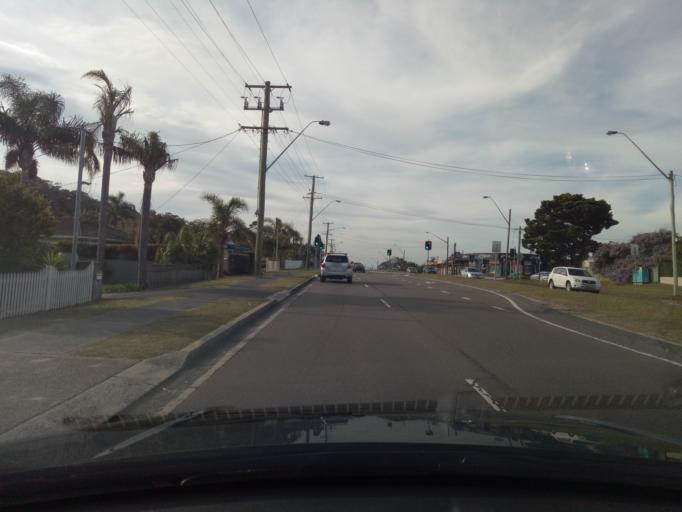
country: AU
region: New South Wales
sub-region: Wyong Shire
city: Bateau Bay
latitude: -33.3901
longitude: 151.4731
